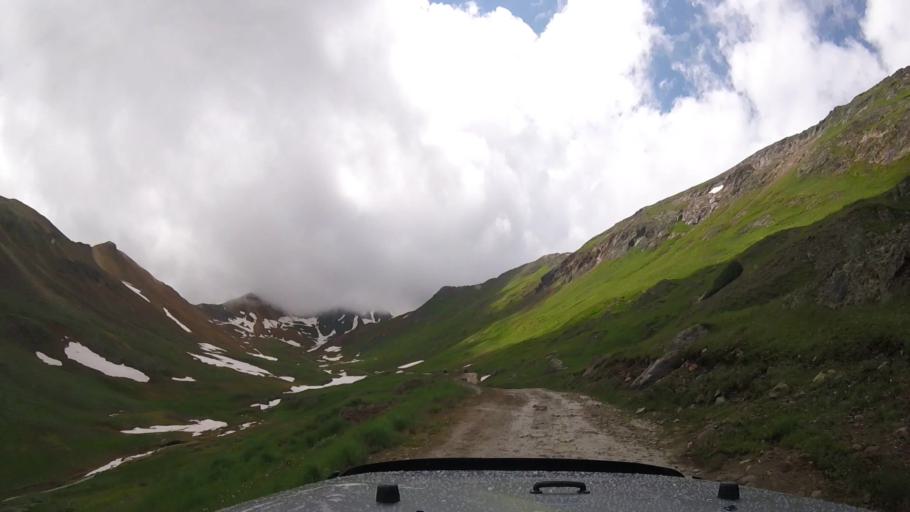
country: US
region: Colorado
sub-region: Ouray County
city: Ouray
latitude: 37.9271
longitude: -107.6087
